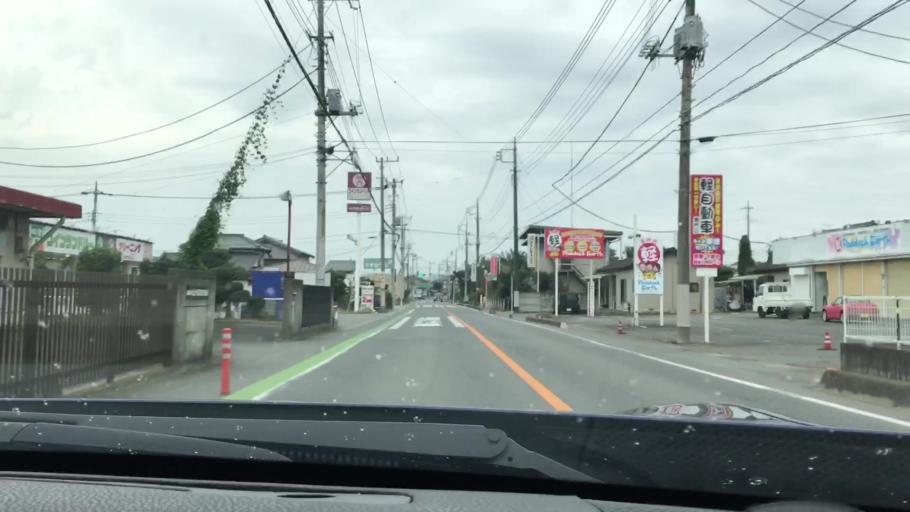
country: JP
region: Gunma
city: Kanekomachi
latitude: 36.3975
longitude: 138.9699
